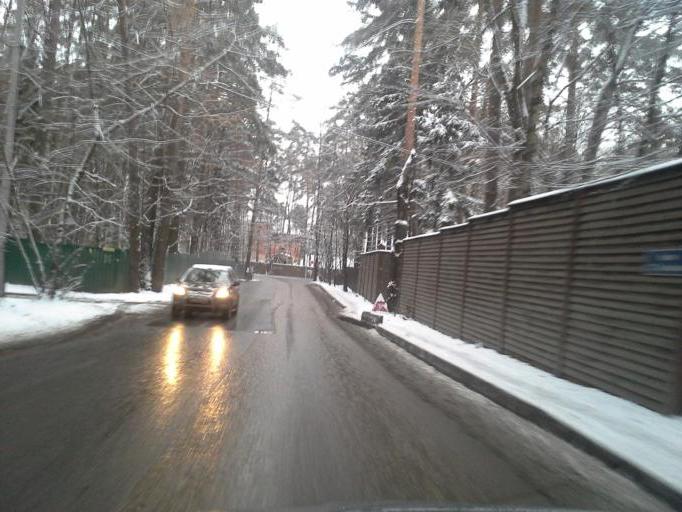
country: RU
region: Moskovskaya
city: Nikolina Gora
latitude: 55.7360
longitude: 37.0376
